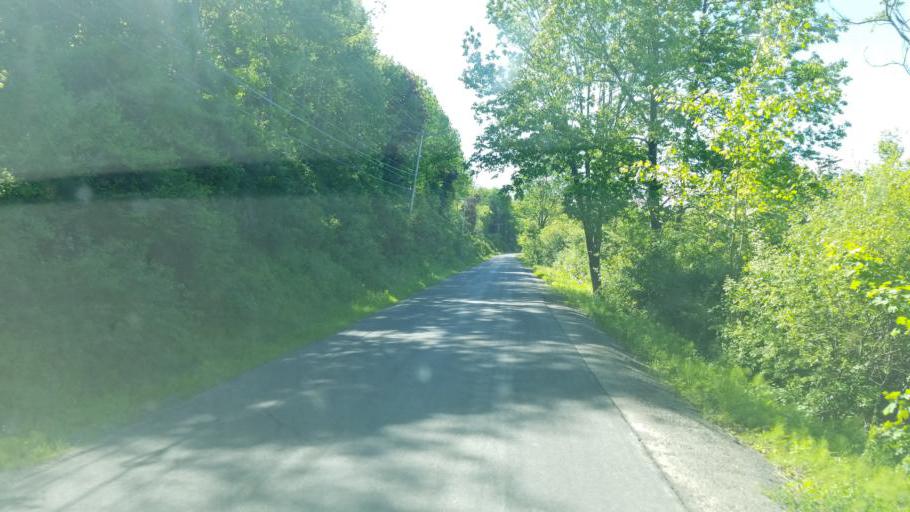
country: US
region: New York
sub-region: Montgomery County
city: Canajoharie
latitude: 42.9072
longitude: -74.5924
